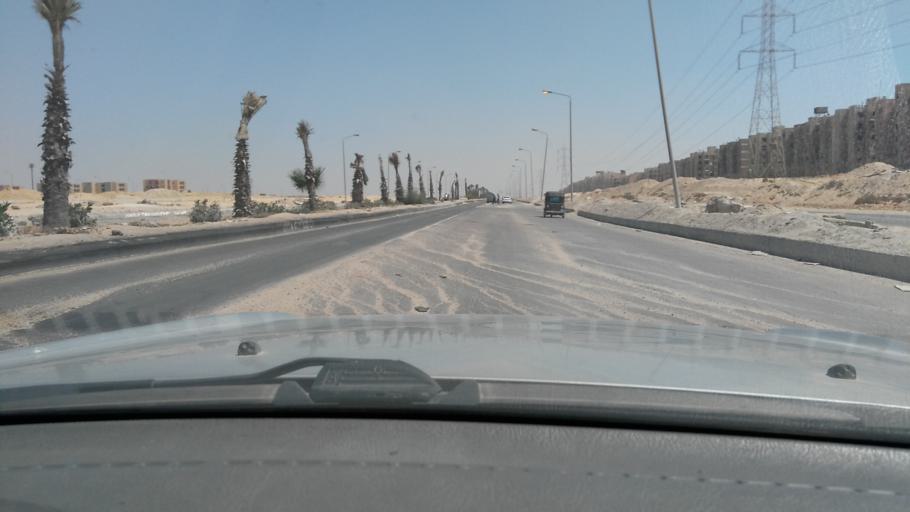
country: EG
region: Al Jizah
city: Madinat Sittah Uktubar
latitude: 29.9181
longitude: 30.9380
